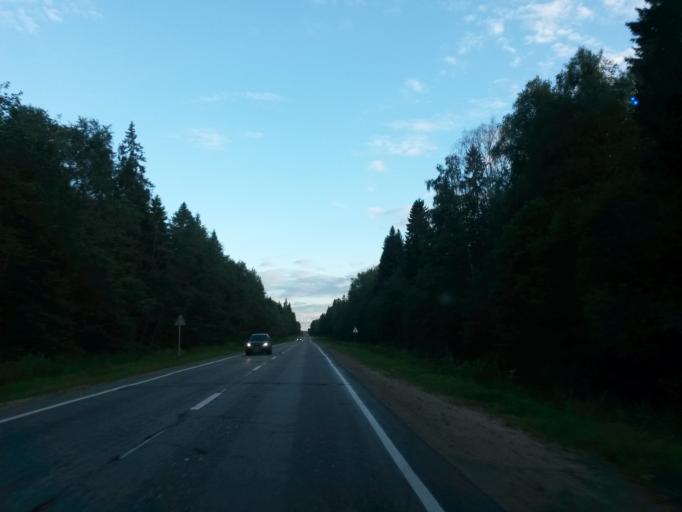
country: RU
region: Jaroslavl
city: Gavrilov-Yam
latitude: 57.4293
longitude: 39.9185
